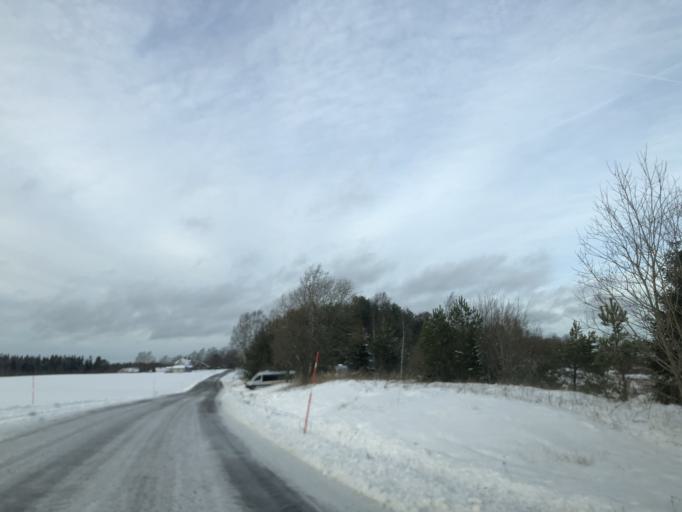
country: SE
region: Vaestra Goetaland
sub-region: Ulricehamns Kommun
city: Ulricehamn
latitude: 57.8146
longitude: 13.5345
